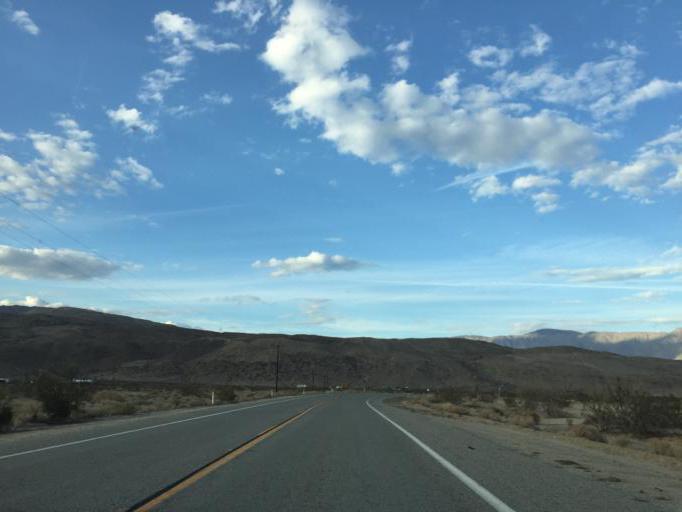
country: US
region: California
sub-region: San Diego County
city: Borrego Springs
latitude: 33.2904
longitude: -116.2985
